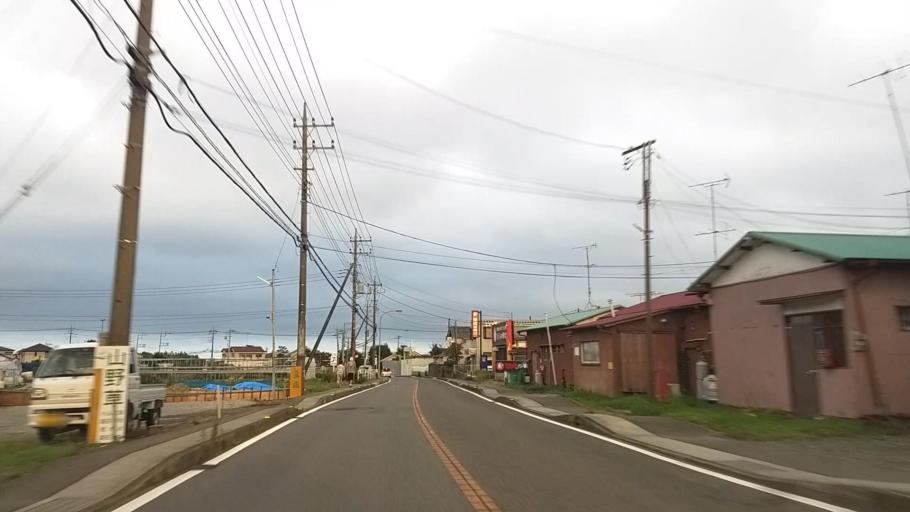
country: JP
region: Kanagawa
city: Atsugi
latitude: 35.4703
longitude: 139.3245
